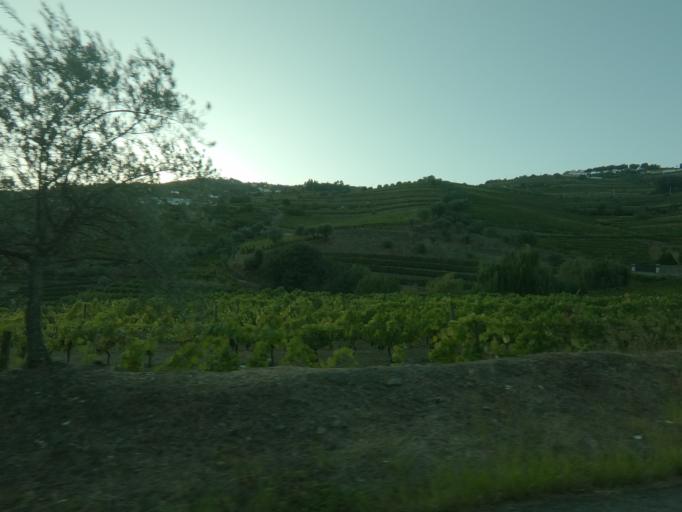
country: PT
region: Vila Real
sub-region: Mesao Frio
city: Mesao Frio
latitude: 41.1763
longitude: -7.8512
